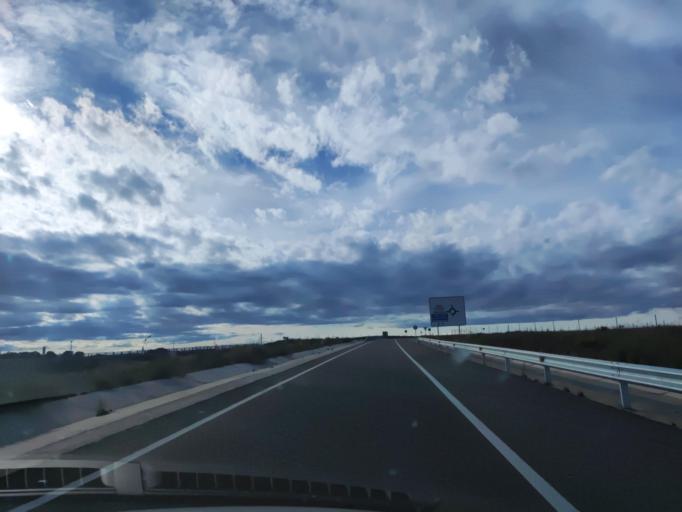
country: ES
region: Castille and Leon
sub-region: Provincia de Salamanca
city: Fuentes de Onoro
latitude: 40.5940
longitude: -6.7947
